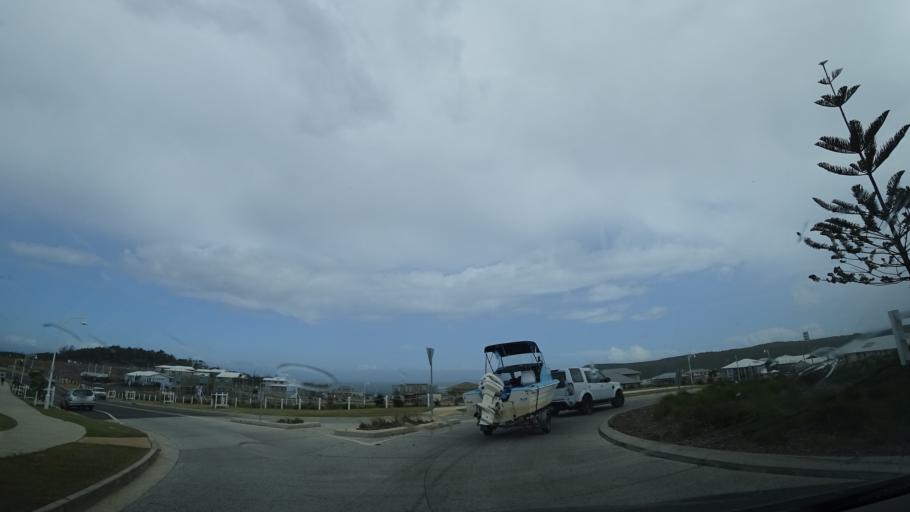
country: AU
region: New South Wales
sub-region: Wyong Shire
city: Kingfisher Shores
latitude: -33.1617
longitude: 151.6273
